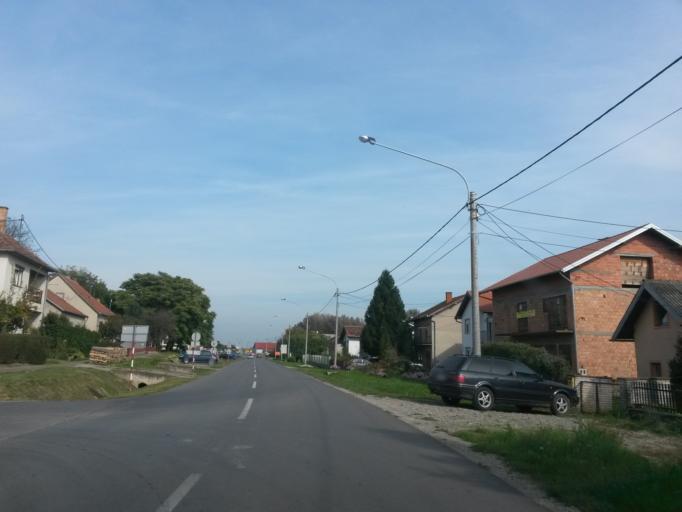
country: HR
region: Osjecko-Baranjska
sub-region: Grad Osijek
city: Bilje
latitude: 45.6065
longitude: 18.7517
